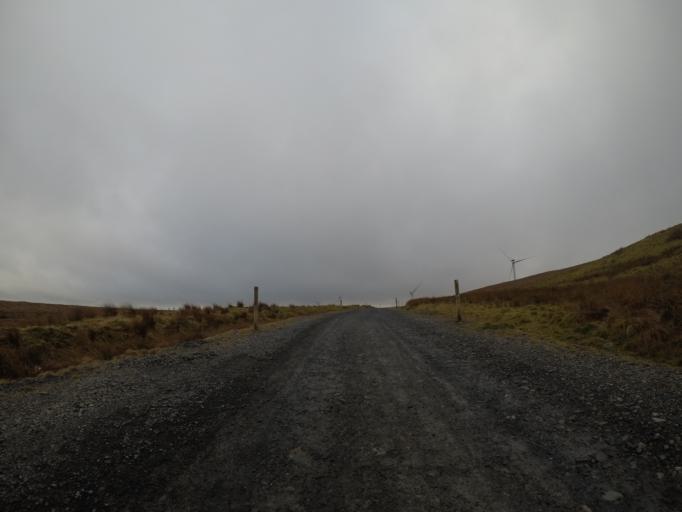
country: GB
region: Scotland
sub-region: North Ayrshire
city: Fairlie
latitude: 55.7613
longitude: -4.7916
